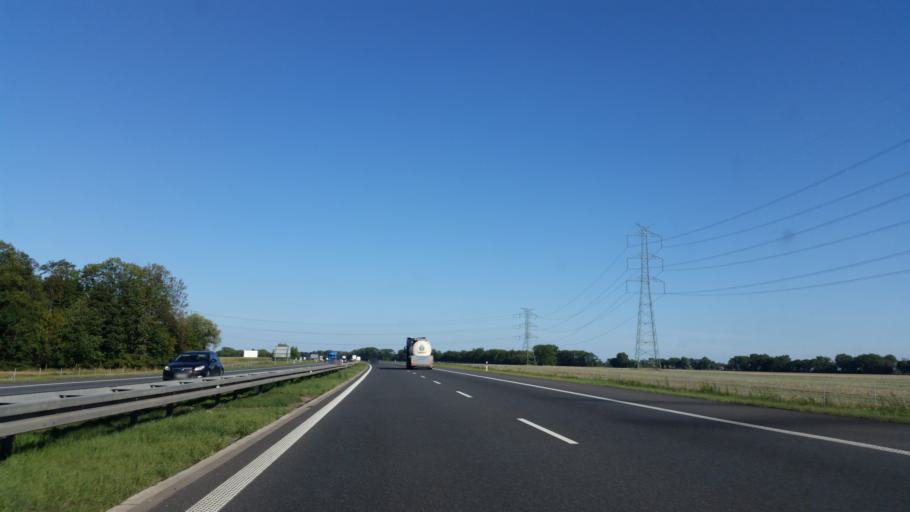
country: PL
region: Opole Voivodeship
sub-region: Powiat brzeski
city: Grodkow
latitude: 50.7742
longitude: 17.3660
